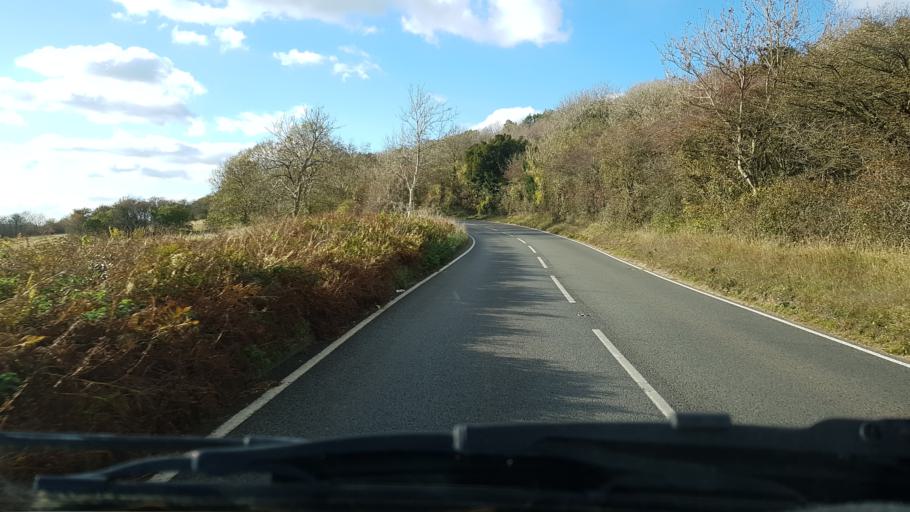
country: GB
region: England
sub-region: Surrey
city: Chilworth
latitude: 51.2309
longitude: -0.4972
